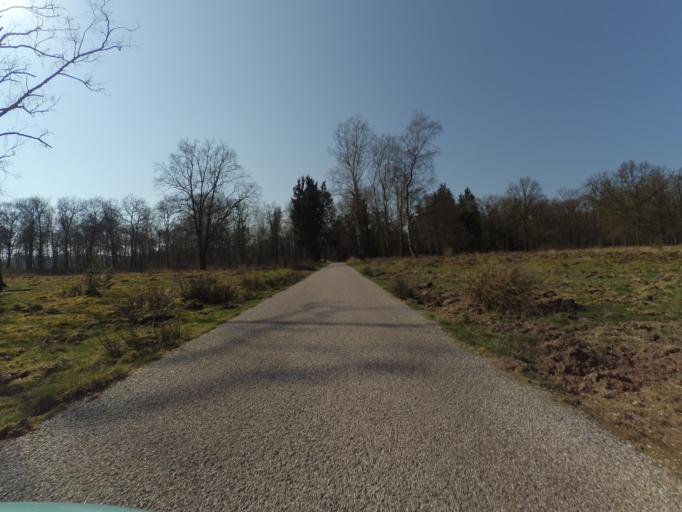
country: NL
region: Gelderland
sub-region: Gemeente Ede
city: Otterlo
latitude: 52.1090
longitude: 5.8416
